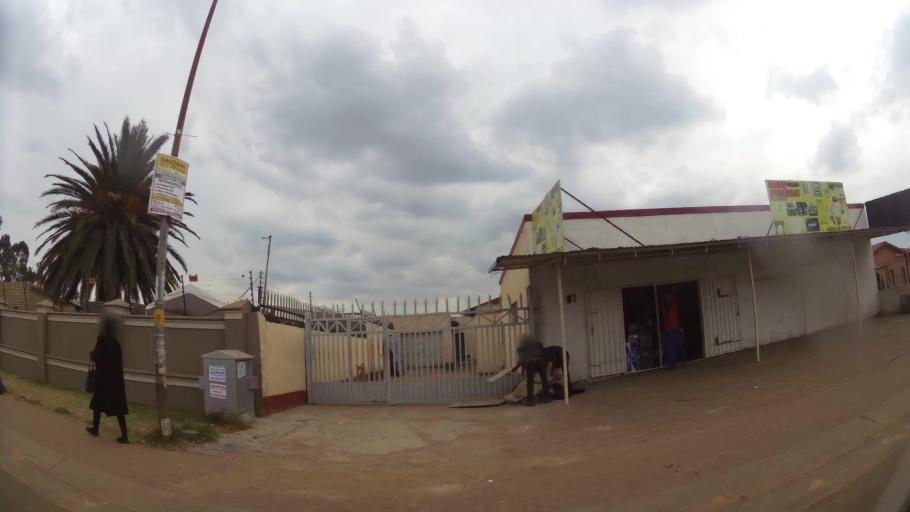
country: ZA
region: Gauteng
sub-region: Ekurhuleni Metropolitan Municipality
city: Germiston
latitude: -26.3906
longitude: 28.1418
